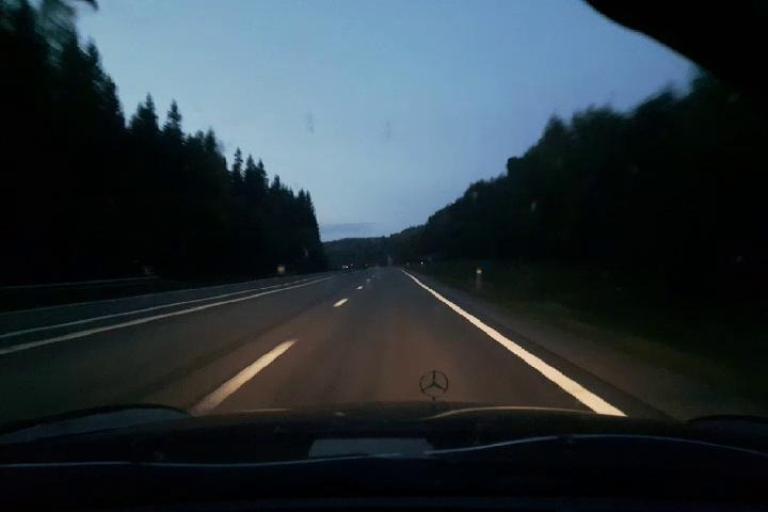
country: SE
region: Vaesternorrland
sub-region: Kramfors Kommun
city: Nordingra
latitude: 63.0791
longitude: 18.3655
